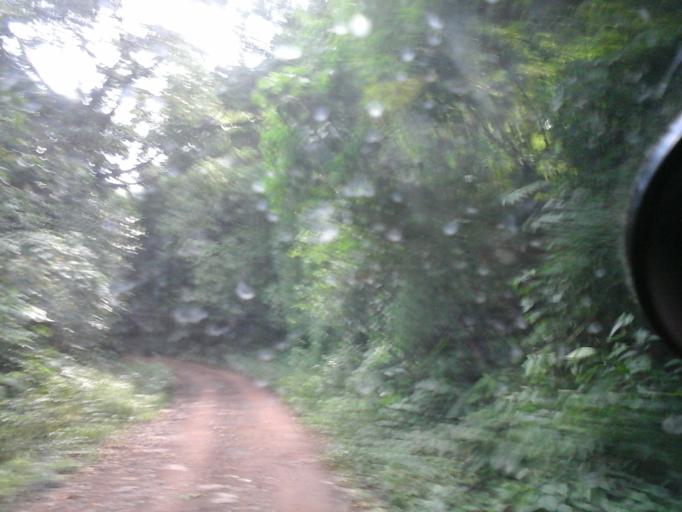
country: CO
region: Cesar
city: San Diego
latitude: 10.2630
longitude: -73.1057
